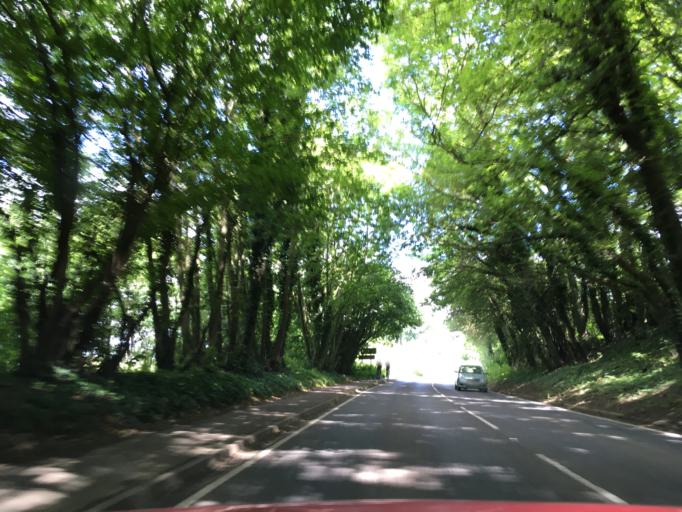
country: GB
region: England
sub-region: Oxfordshire
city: Bloxham
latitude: 52.0365
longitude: -1.3642
